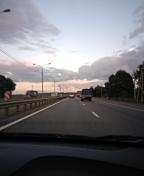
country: RU
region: Moskovskaya
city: Zhukovskiy
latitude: 55.5221
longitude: 38.1204
